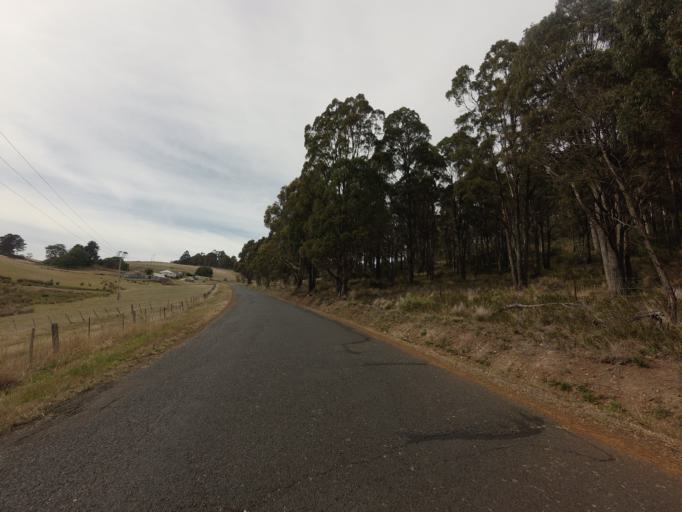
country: AU
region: Tasmania
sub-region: Sorell
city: Sorell
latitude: -42.4435
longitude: 147.5394
